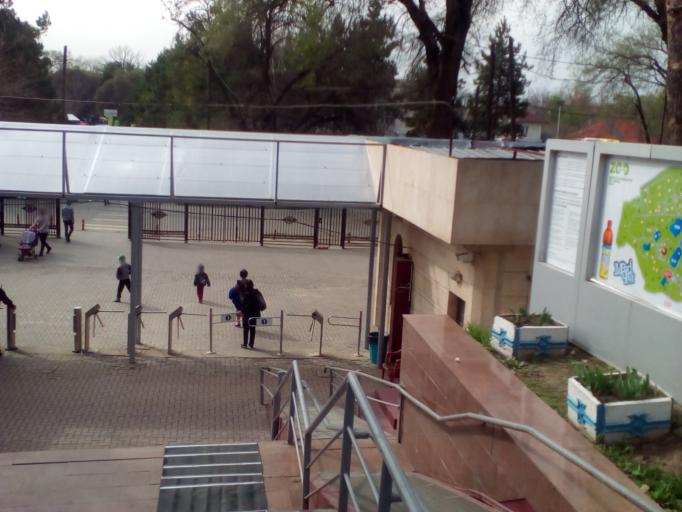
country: KZ
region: Almaty Qalasy
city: Almaty
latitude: 43.2635
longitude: 76.9743
